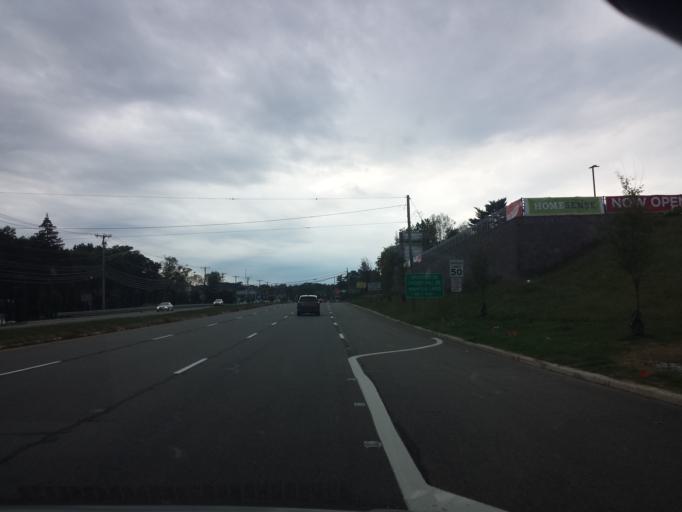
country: US
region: New Jersey
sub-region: Morris County
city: Parsippany
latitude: 40.8735
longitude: -74.4312
